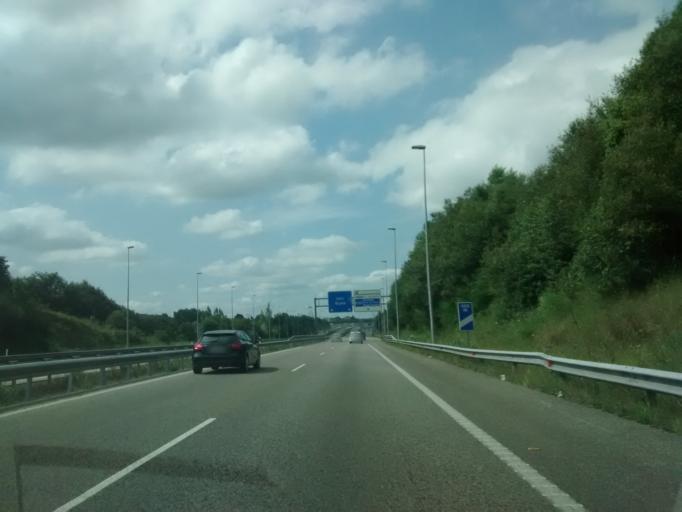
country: ES
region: Asturias
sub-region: Province of Asturias
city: Pola de Siero
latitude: 43.3740
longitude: -5.6834
